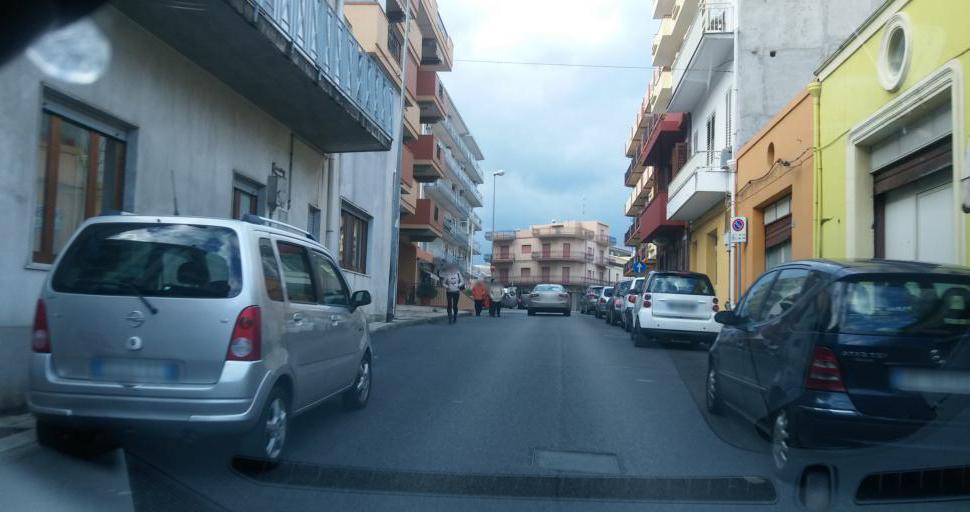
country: IT
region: Sicily
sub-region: Messina
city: Milazzo
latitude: 38.2195
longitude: 15.2374
